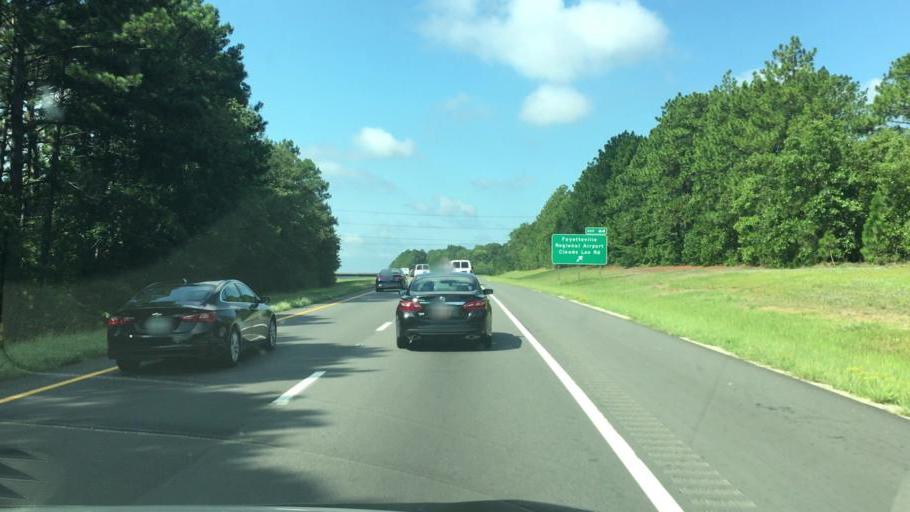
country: US
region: North Carolina
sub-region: Cumberland County
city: Hope Mills
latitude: 34.9663
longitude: -78.8845
